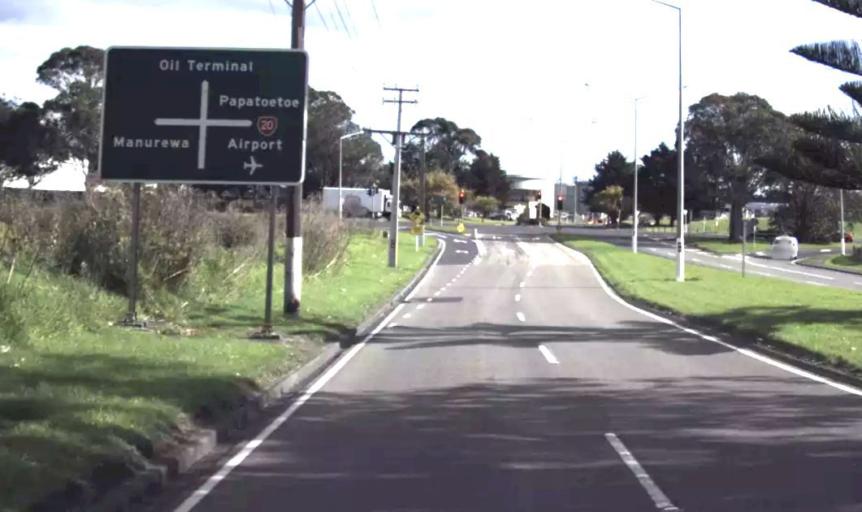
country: NZ
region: Auckland
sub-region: Auckland
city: Wiri
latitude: -37.0056
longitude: 174.8566
